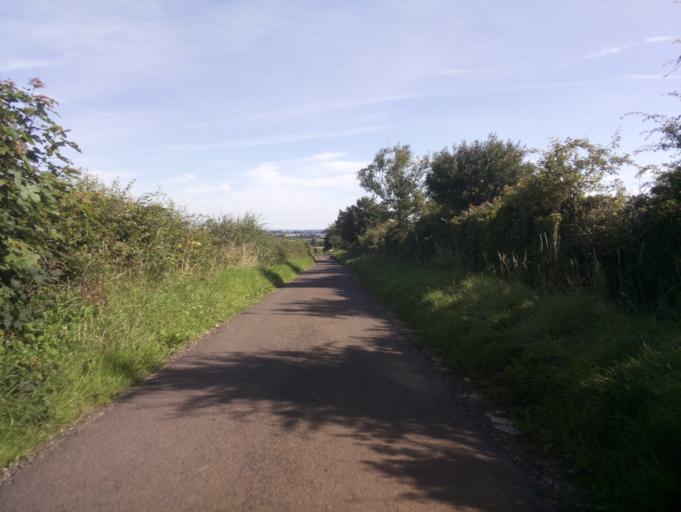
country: GB
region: England
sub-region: Bath and North East Somerset
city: Publow
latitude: 51.3916
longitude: -2.5326
